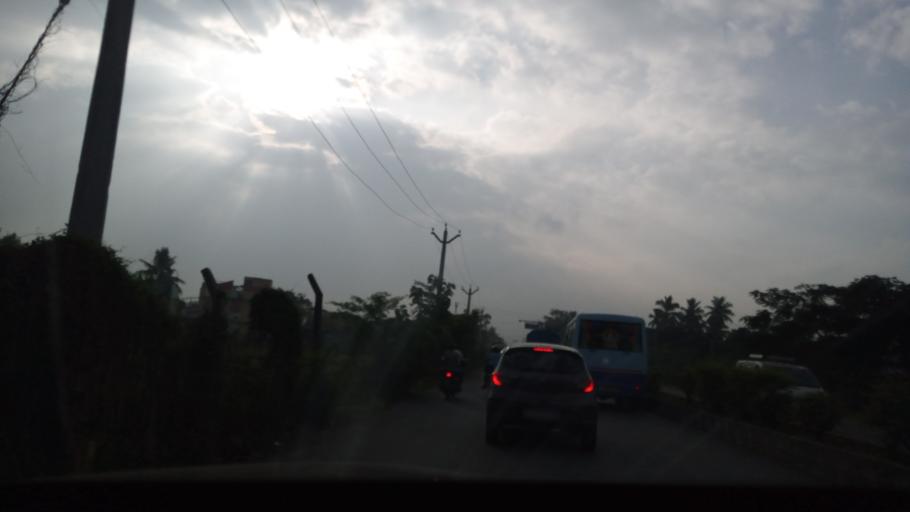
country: IN
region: Tamil Nadu
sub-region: Kancheepuram
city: Vengavasal
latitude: 12.8592
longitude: 80.1326
